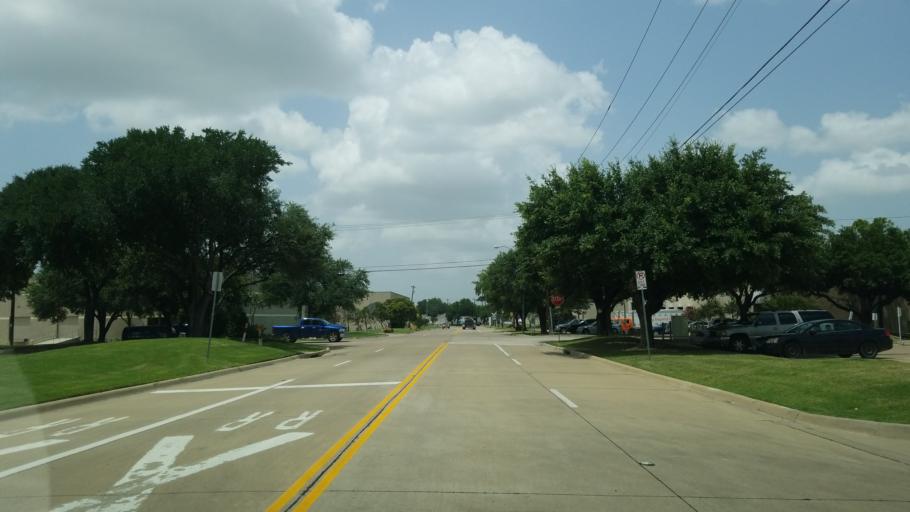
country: US
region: Texas
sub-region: Dallas County
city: Cockrell Hill
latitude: 32.7705
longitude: -96.8844
